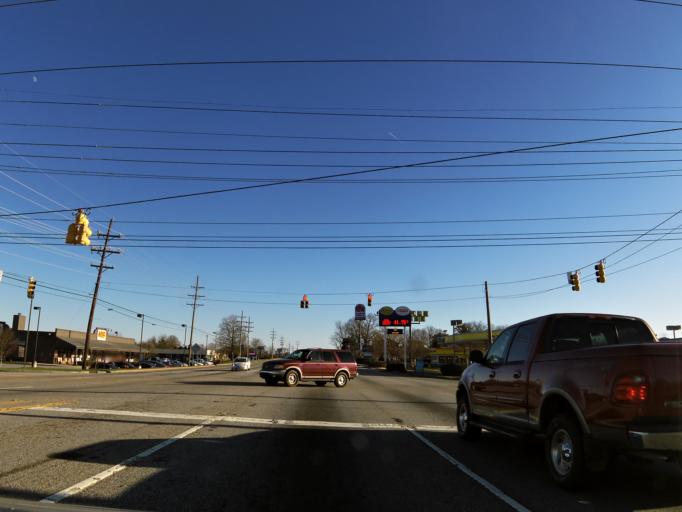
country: US
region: South Carolina
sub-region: Spartanburg County
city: Wellford
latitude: 34.9108
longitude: -82.1040
